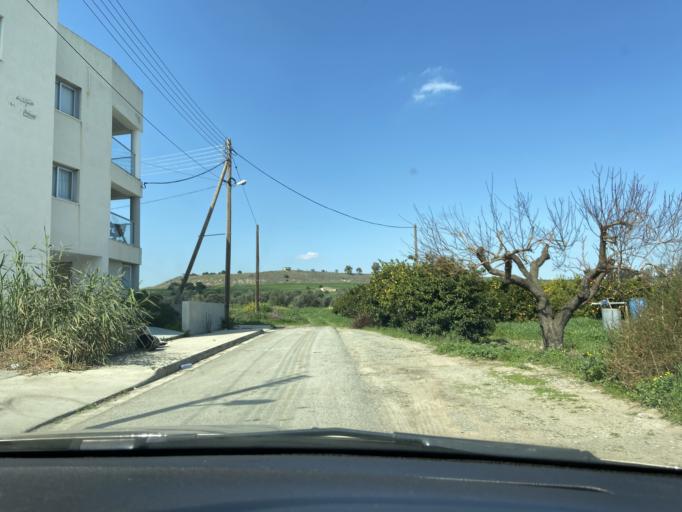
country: CY
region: Lefkosia
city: Dali
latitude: 35.0233
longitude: 33.3891
